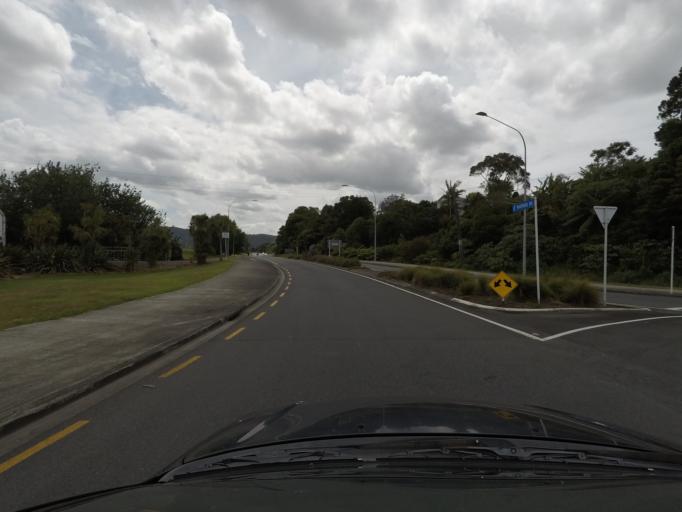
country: NZ
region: Northland
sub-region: Whangarei
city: Whangarei
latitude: -35.7311
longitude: 174.3424
